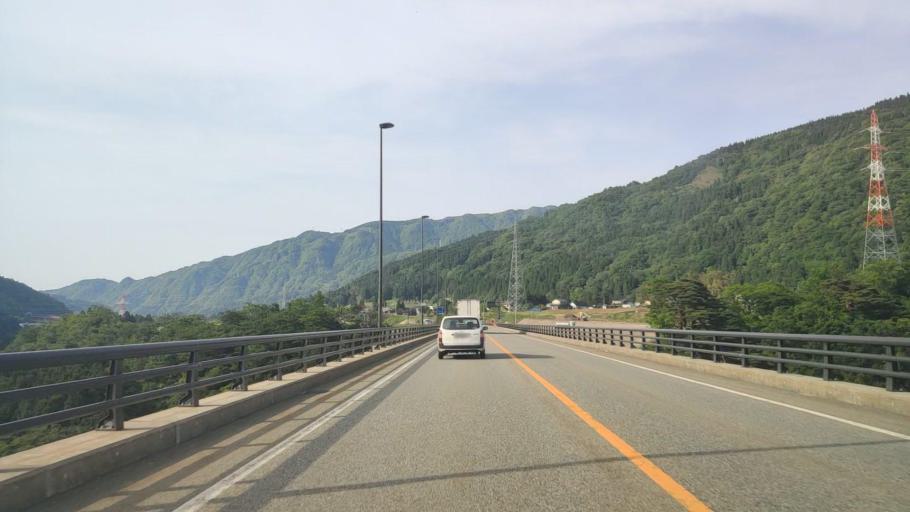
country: JP
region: Toyama
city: Yatsuomachi-higashikumisaka
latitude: 36.5150
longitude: 137.2292
